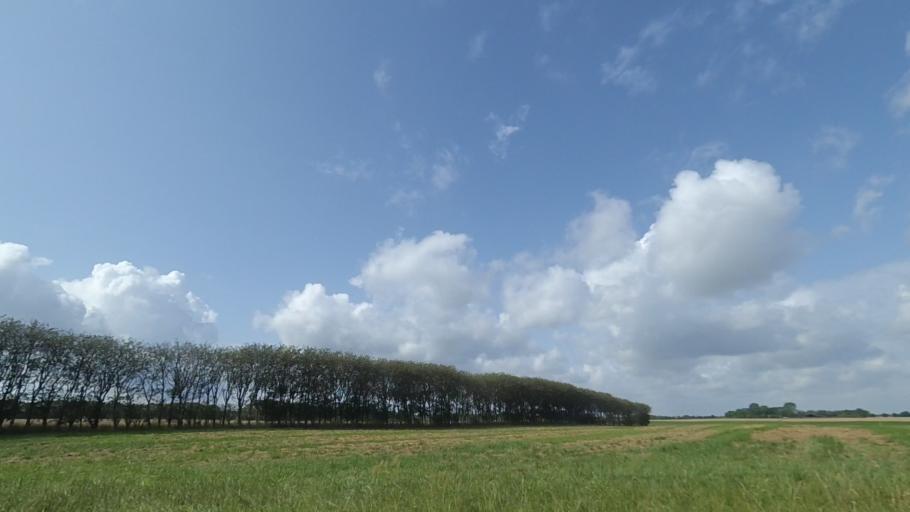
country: DK
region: Central Jutland
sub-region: Syddjurs Kommune
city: Ryomgard
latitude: 56.4715
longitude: 10.5102
